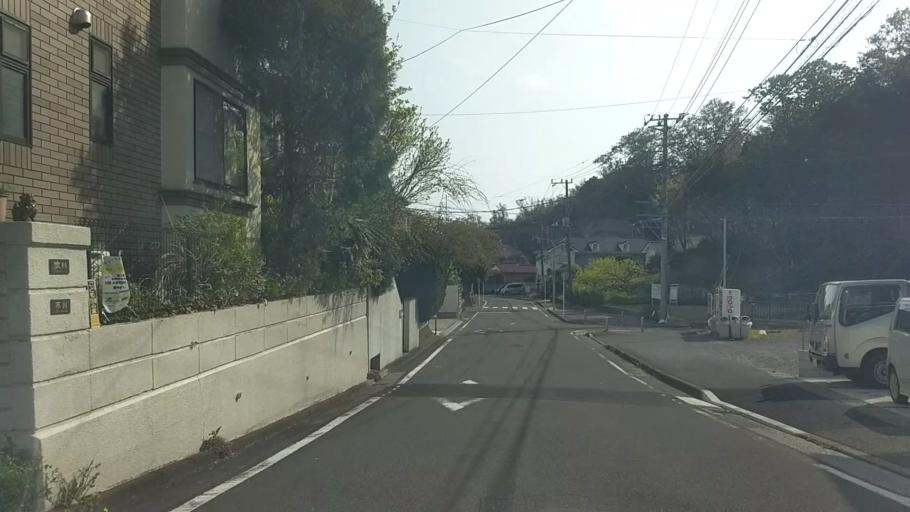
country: JP
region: Kanagawa
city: Kamakura
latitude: 35.3760
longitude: 139.5551
